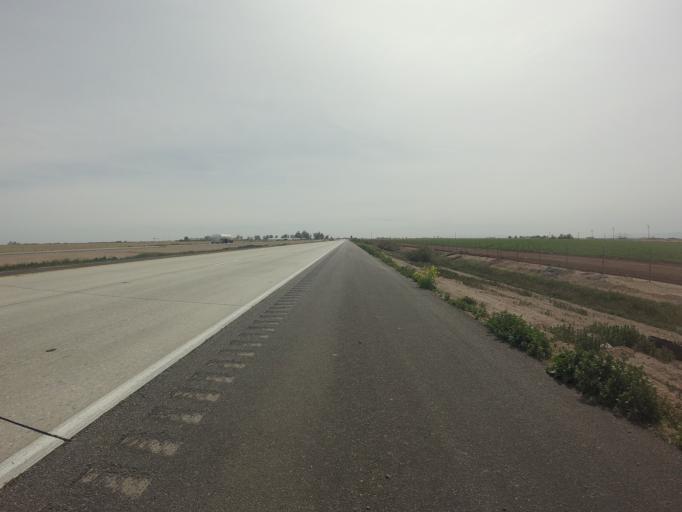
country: US
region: California
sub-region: Imperial County
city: Westmorland
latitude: 33.0205
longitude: -115.6033
